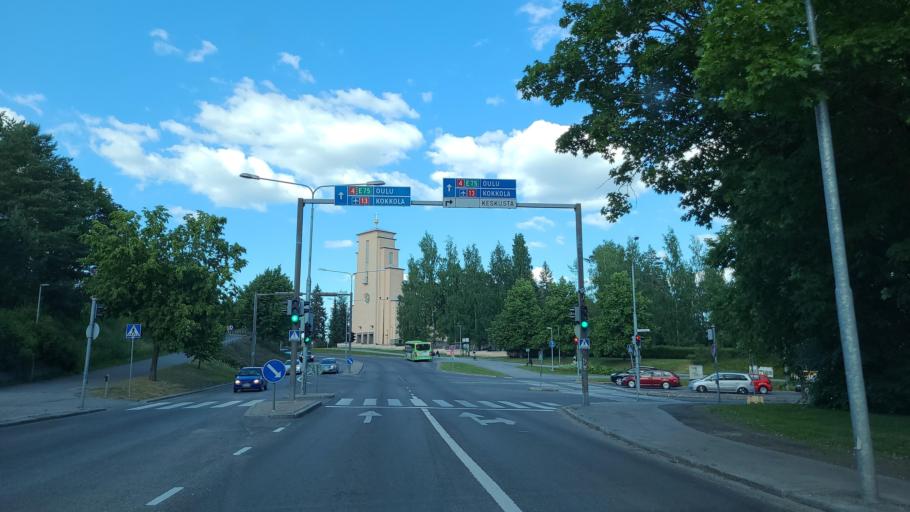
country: FI
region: Central Finland
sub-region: Jyvaeskylae
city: Jyvaeskylae
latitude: 62.2523
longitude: 25.7482
